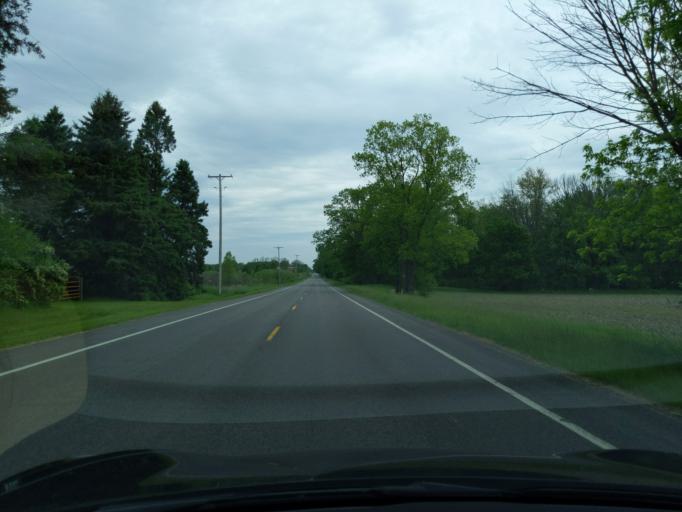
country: US
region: Michigan
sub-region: Ingham County
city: Mason
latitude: 42.5586
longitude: -84.3568
